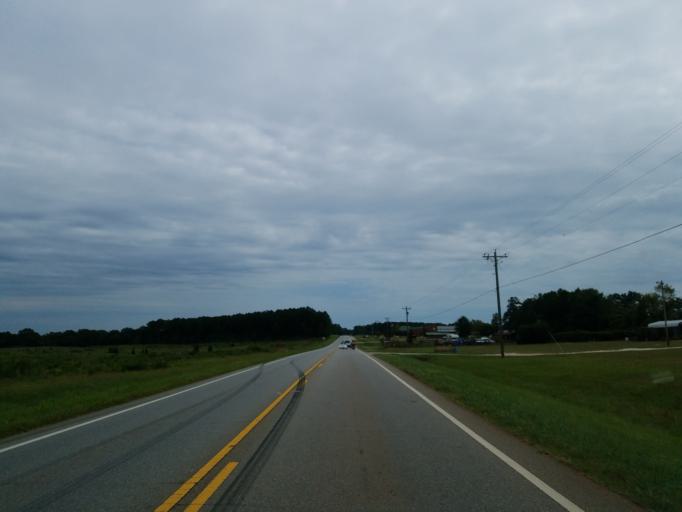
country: US
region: Georgia
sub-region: Lamar County
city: Barnesville
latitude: 33.0174
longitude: -84.1323
